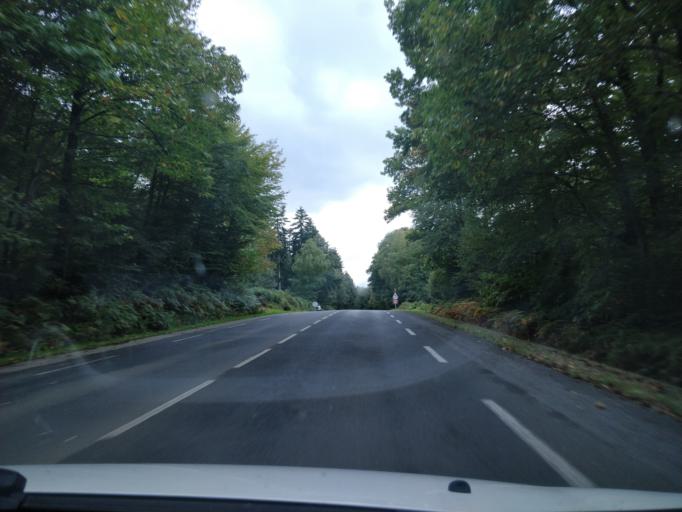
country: FR
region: Lower Normandy
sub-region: Departement du Calvados
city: Saint-Sever-Calvados
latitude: 48.8313
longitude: -1.0755
